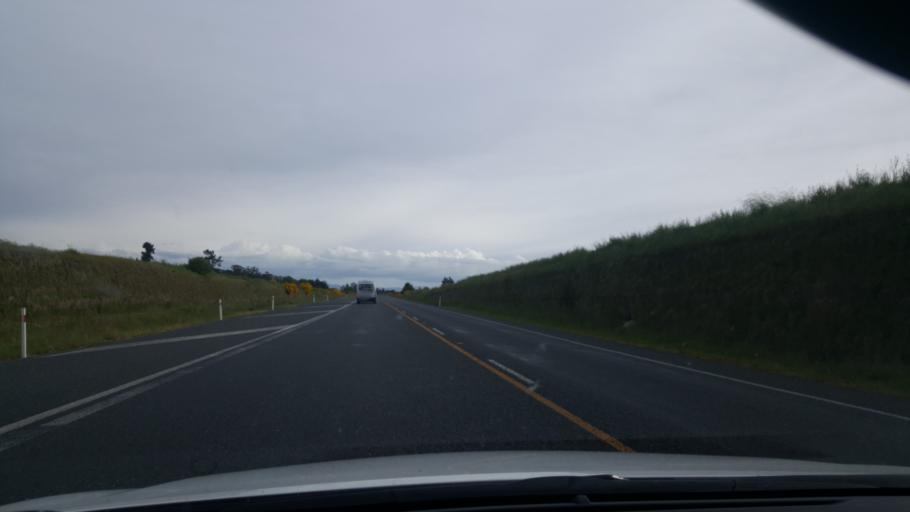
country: NZ
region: Waikato
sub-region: Taupo District
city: Taupo
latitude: -38.6509
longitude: 176.1003
